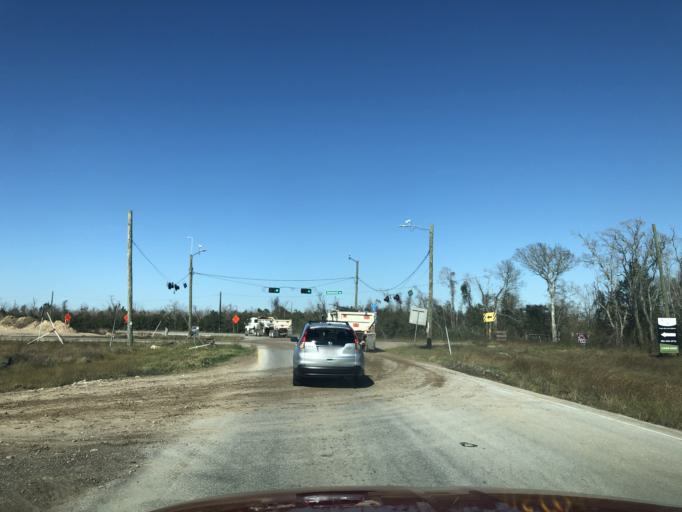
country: US
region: Texas
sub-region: Galveston County
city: Dickinson
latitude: 29.4298
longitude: -95.0574
